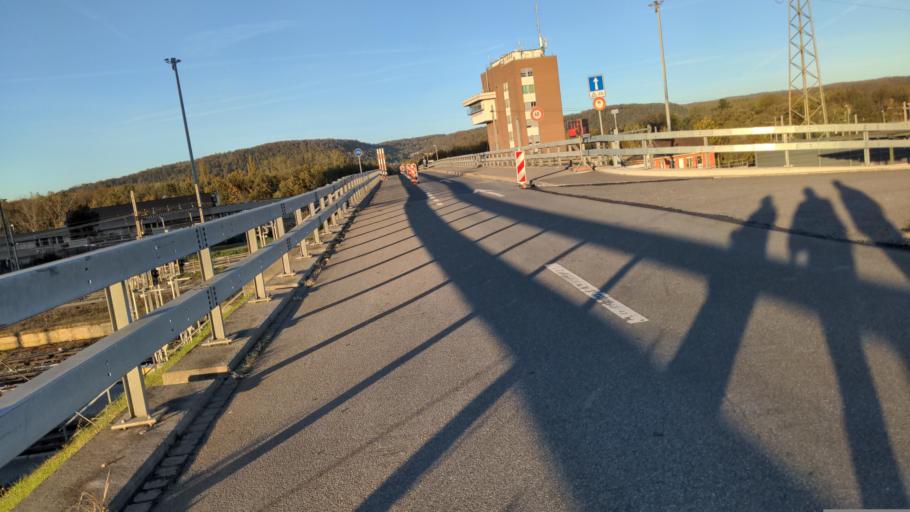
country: CH
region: Basel-Landschaft
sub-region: Bezirk Arlesheim
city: Muttenz
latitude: 47.5349
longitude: 7.6450
